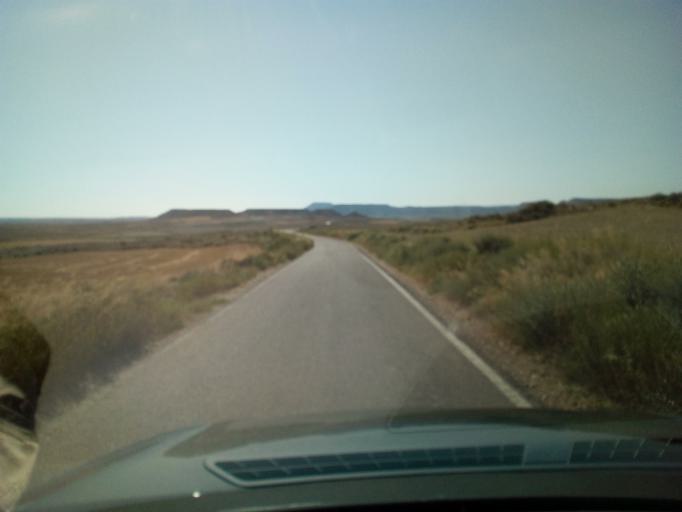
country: ES
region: Navarre
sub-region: Provincia de Navarra
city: Arguedas
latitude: 42.1797
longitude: -1.5249
